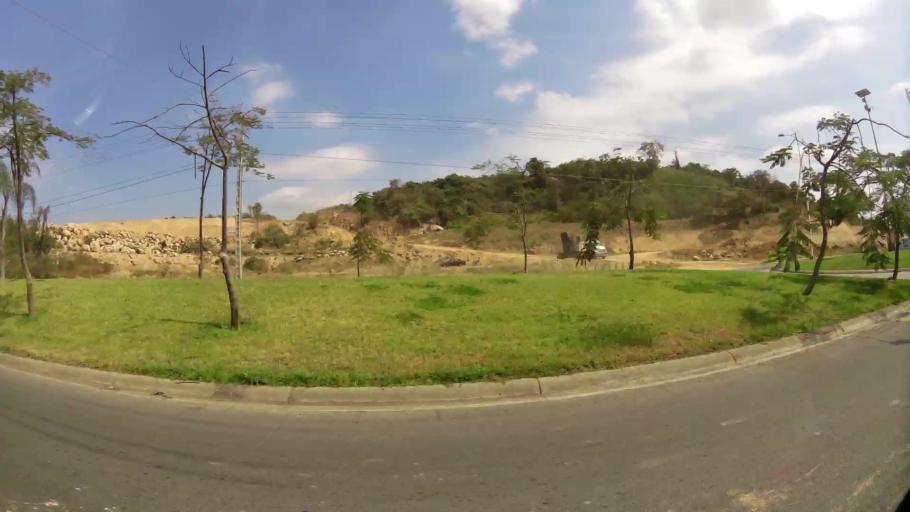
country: EC
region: Guayas
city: El Triunfo
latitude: -2.0305
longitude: -79.9032
